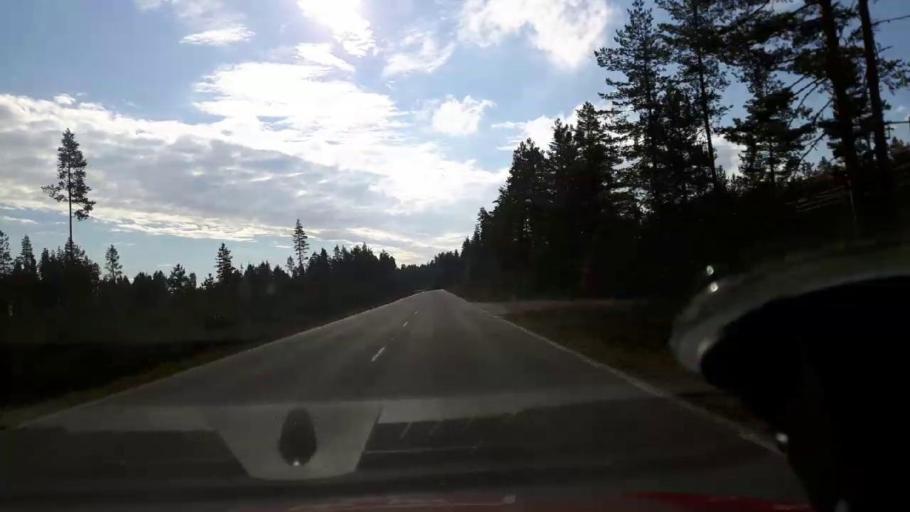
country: SE
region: Vaesternorrland
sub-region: Ange Kommun
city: Ange
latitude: 62.0637
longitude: 15.1110
